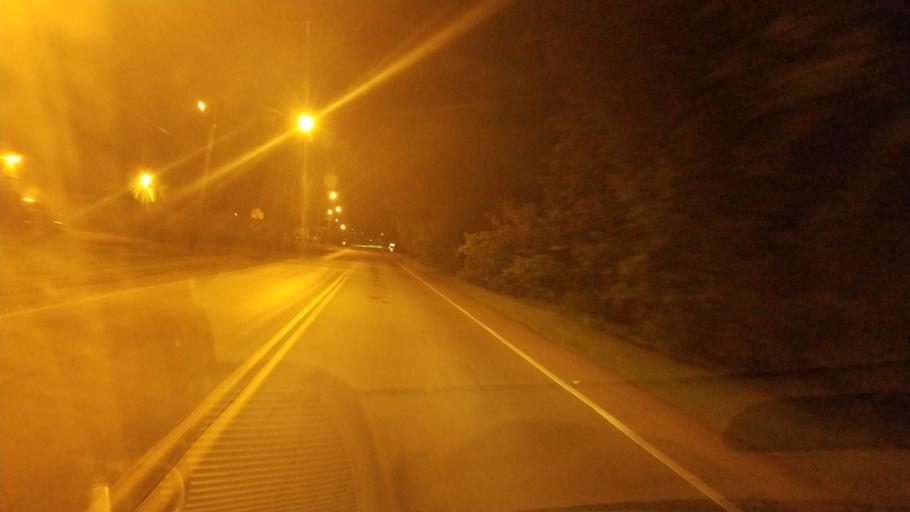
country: US
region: Ohio
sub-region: Trumbull County
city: Niles
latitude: 41.1679
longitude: -80.7663
